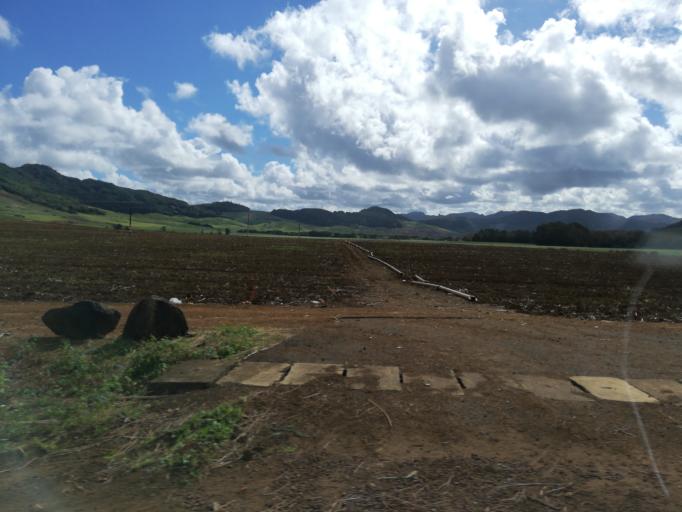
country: MU
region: Grand Port
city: Bois des Amourettes
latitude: -20.3737
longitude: 57.7000
